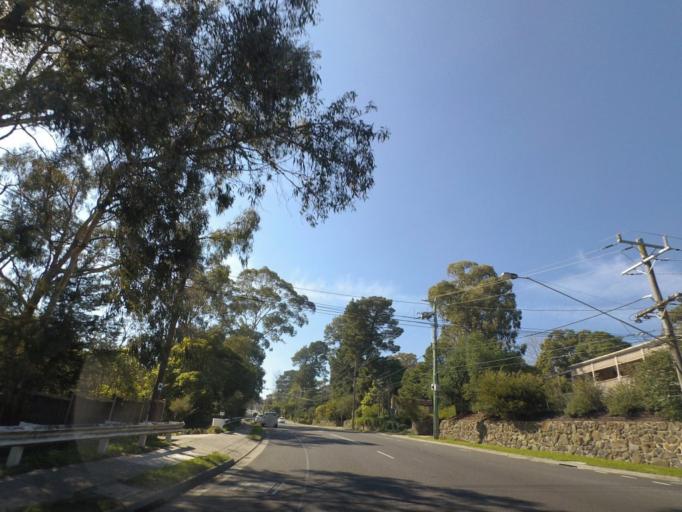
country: AU
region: Victoria
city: Mitcham
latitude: -37.8103
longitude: 145.2162
